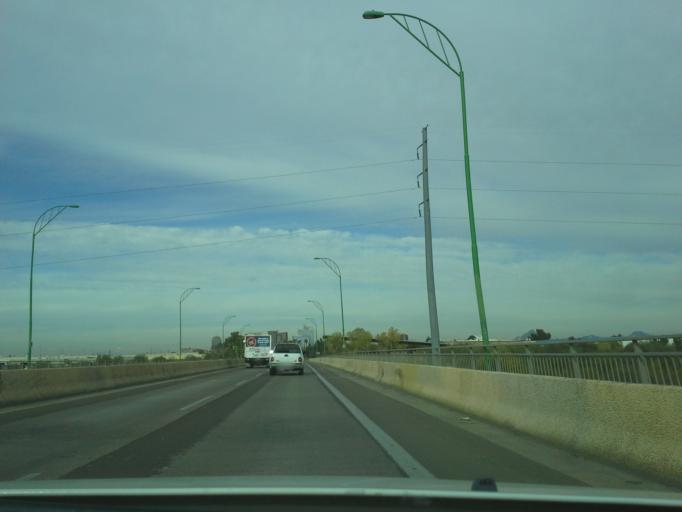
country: US
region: Arizona
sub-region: Maricopa County
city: Phoenix
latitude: 33.4213
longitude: -112.0732
